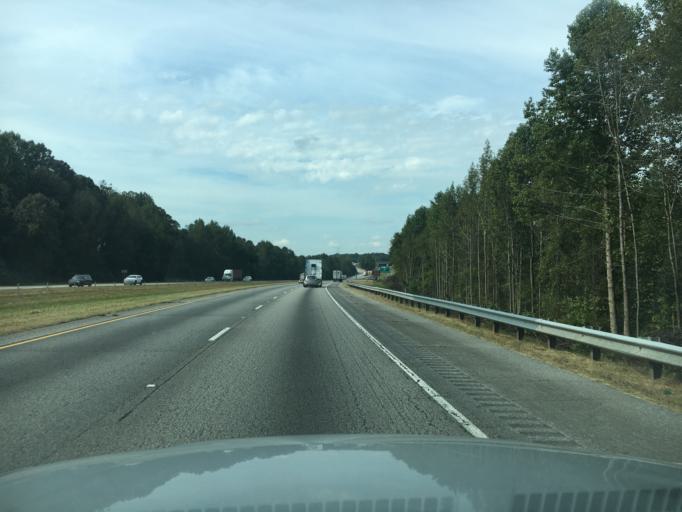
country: US
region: Georgia
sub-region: Franklin County
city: Carnesville
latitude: 34.3507
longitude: -83.3088
